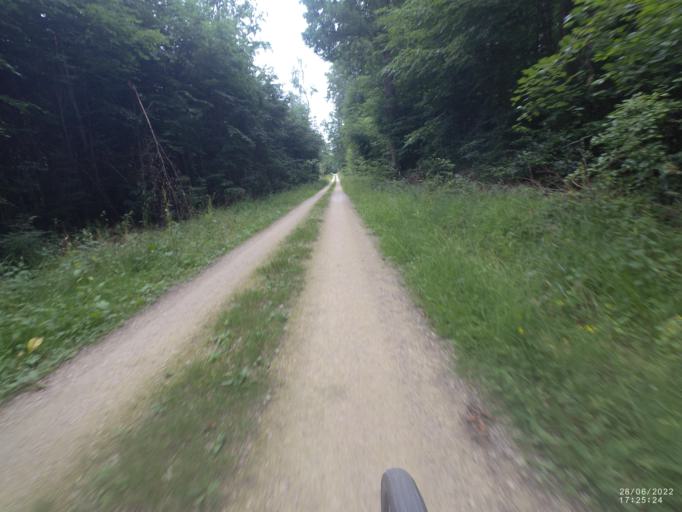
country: DE
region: Baden-Wuerttemberg
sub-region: Regierungsbezirk Stuttgart
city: Gerstetten
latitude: 48.6524
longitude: 10.0376
